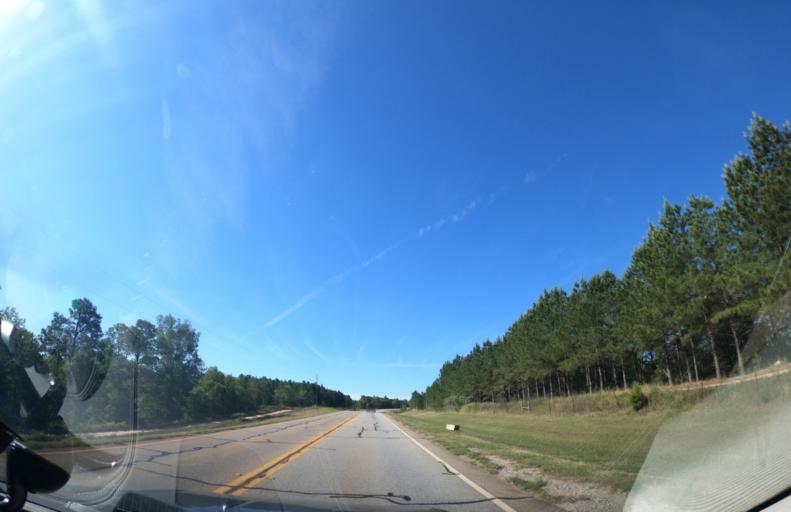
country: US
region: Georgia
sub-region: Jefferson County
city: Wrens
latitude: 33.2996
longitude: -82.3766
